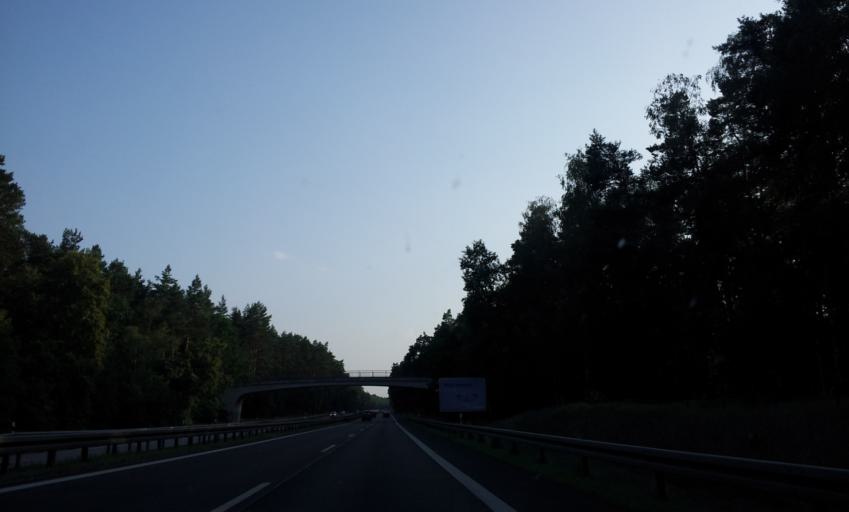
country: DE
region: Brandenburg
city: Marienwerder
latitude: 52.8306
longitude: 13.6573
